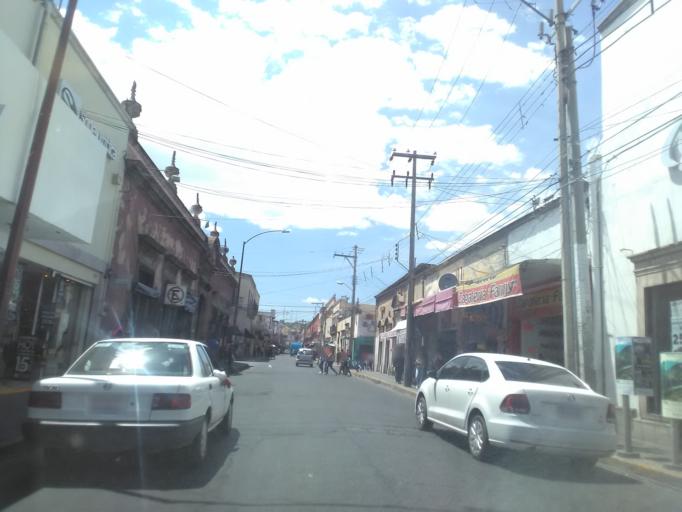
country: MX
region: Durango
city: Victoria de Durango
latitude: 24.0241
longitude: -104.6651
